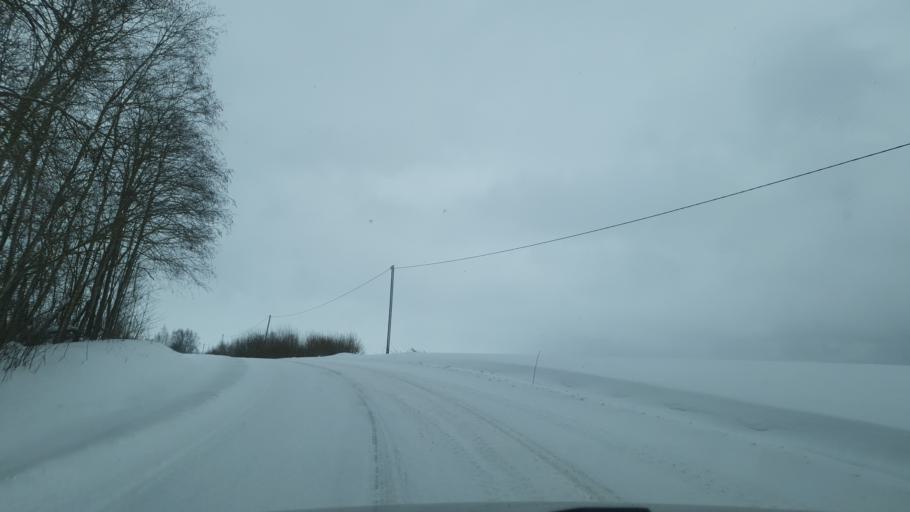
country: EE
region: Polvamaa
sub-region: Raepina vald
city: Rapina
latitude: 58.1610
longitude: 27.3741
